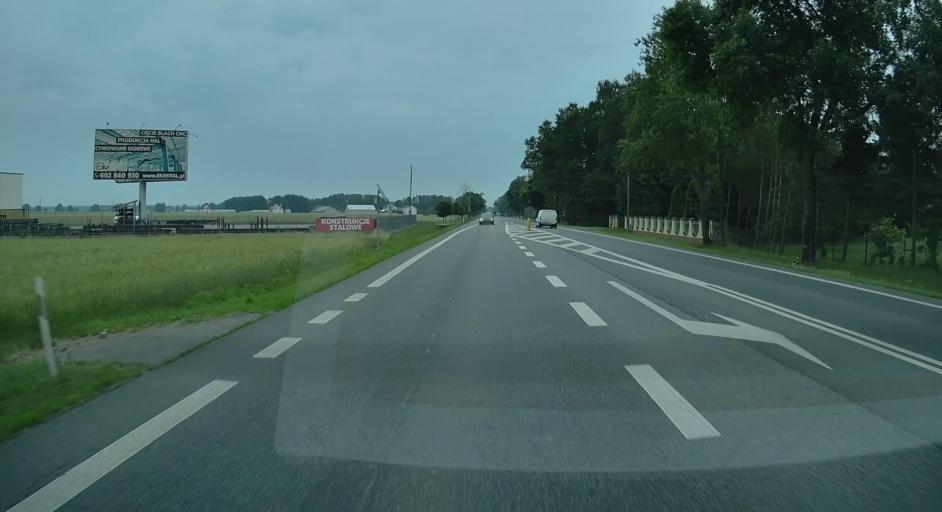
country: PL
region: Masovian Voivodeship
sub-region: Powiat siedlecki
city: Zbuczyn
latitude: 52.0960
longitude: 22.4157
